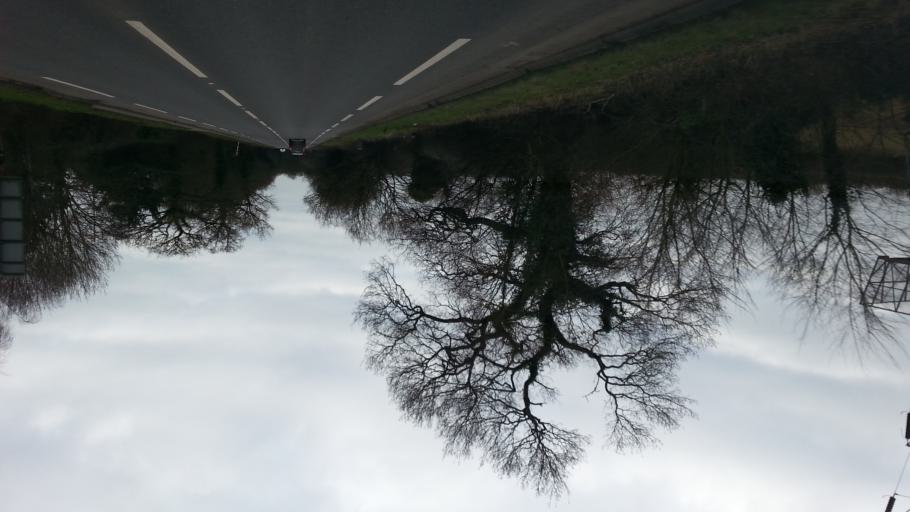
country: GB
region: England
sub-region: Solihull
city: Chelmsley Wood
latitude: 52.4728
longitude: -1.7190
